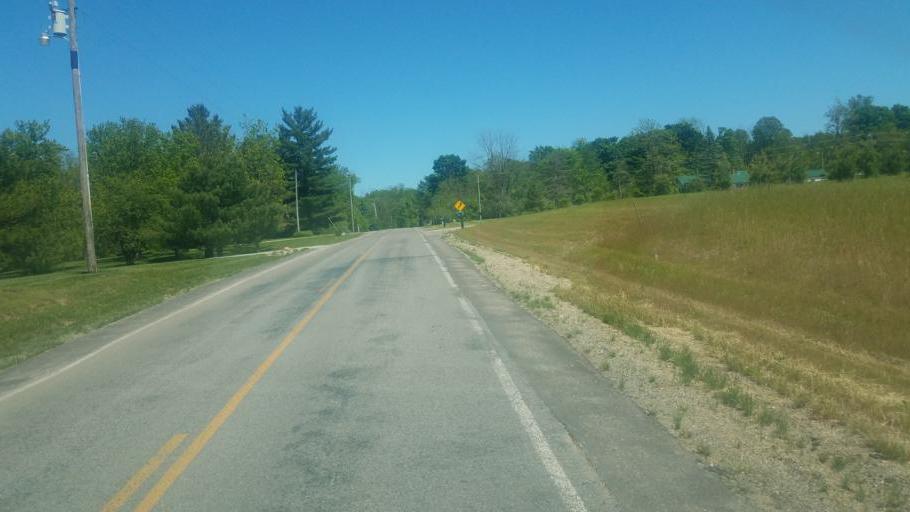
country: US
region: Ohio
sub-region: Champaign County
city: Saint Paris
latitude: 40.1756
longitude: -83.9683
